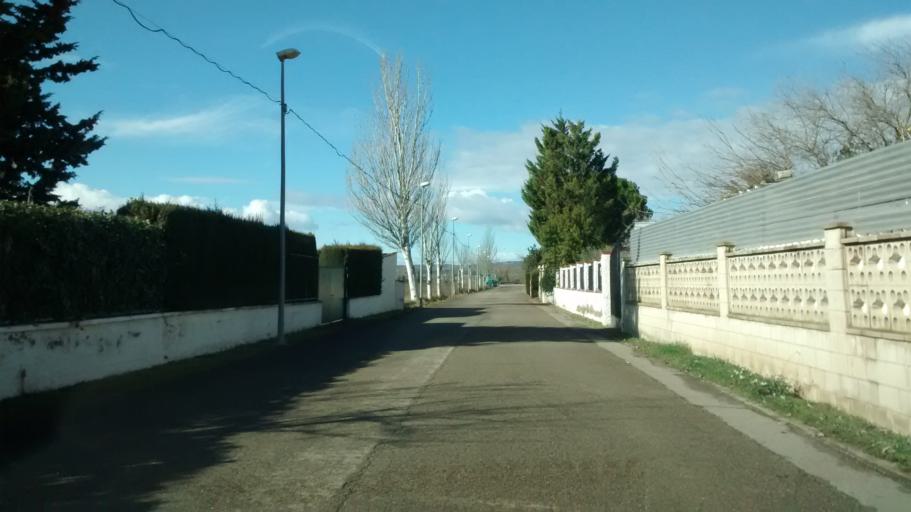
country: ES
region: Aragon
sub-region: Provincia de Zaragoza
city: Villanueva de Gallego
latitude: 41.7348
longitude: -0.8060
